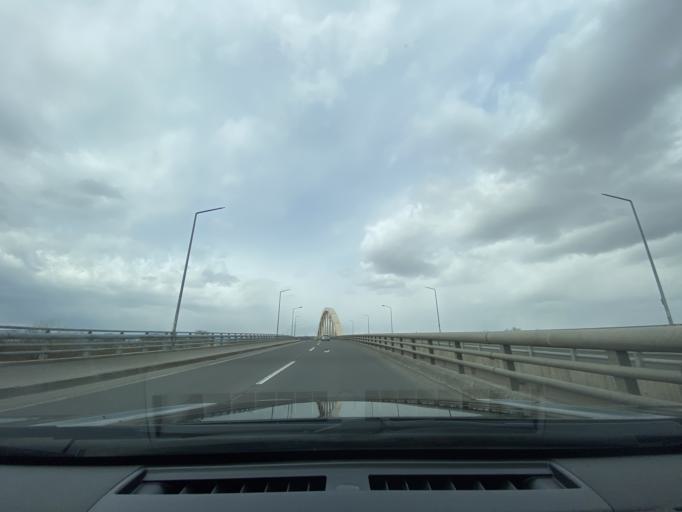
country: JP
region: Hokkaido
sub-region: Asahikawa-shi
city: Asahikawa
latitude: 43.8114
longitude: 142.4111
